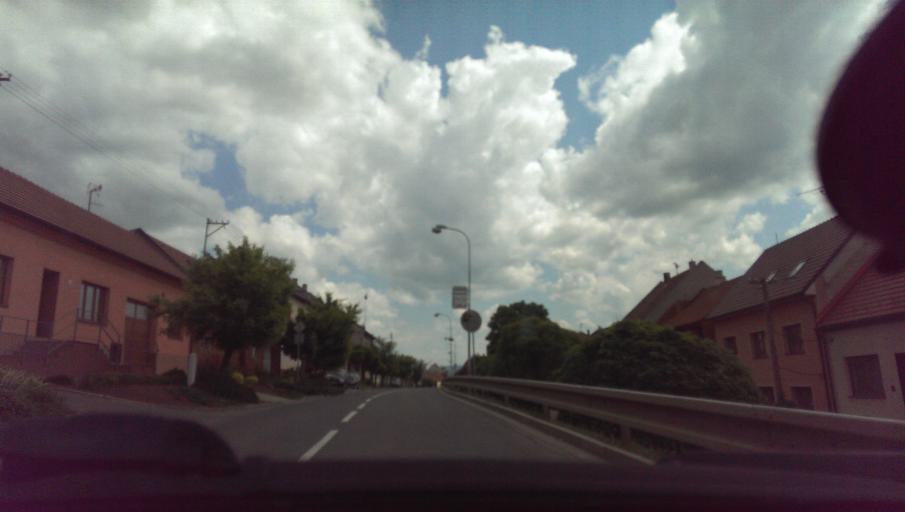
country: CZ
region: Zlin
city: Dolni Nemci
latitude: 48.9690
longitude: 17.5782
